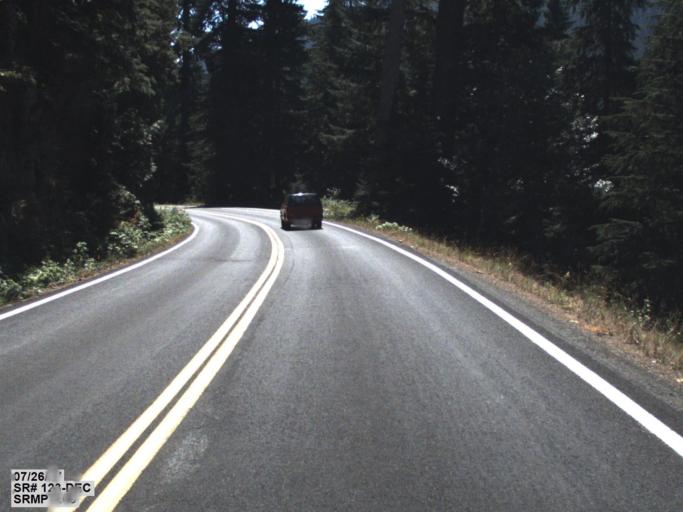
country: US
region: Washington
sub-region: King County
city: Enumclaw
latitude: 46.8135
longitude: -121.5563
